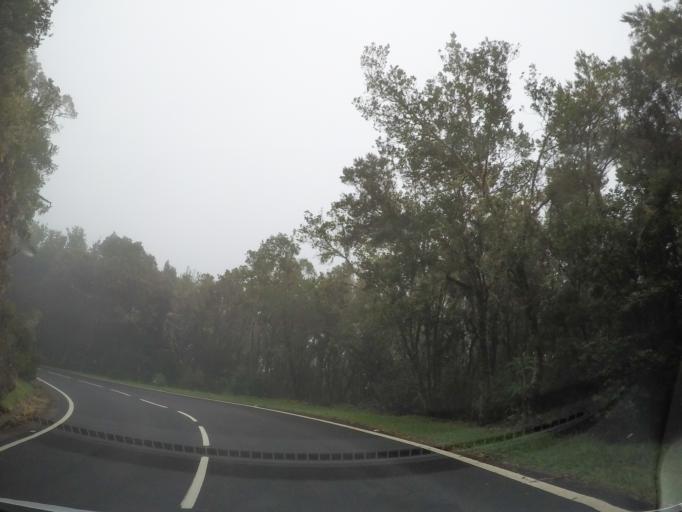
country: ES
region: Canary Islands
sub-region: Provincia de Santa Cruz de Tenerife
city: Vallehermosa
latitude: 28.1408
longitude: -17.2839
